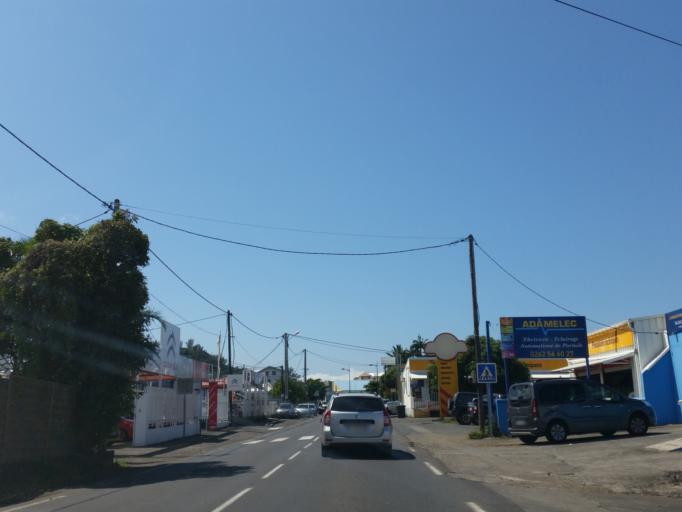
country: RE
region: Reunion
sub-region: Reunion
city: Saint-Joseph
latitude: -21.3808
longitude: 55.6104
